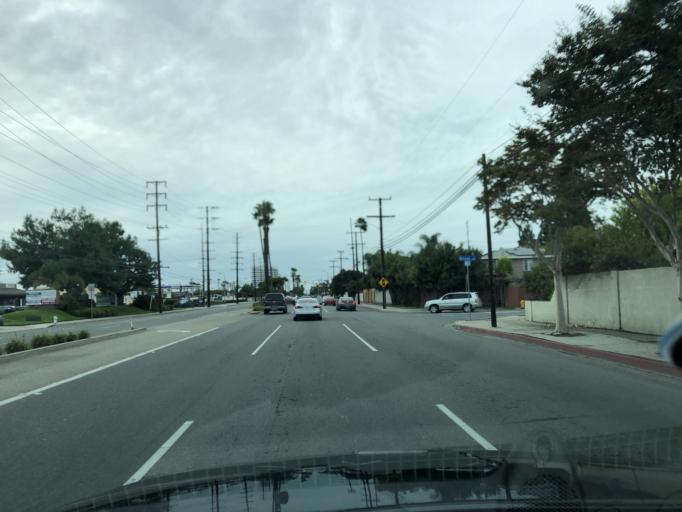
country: US
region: California
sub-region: Orange County
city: Fountain Valley
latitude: 33.7158
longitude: -117.9783
